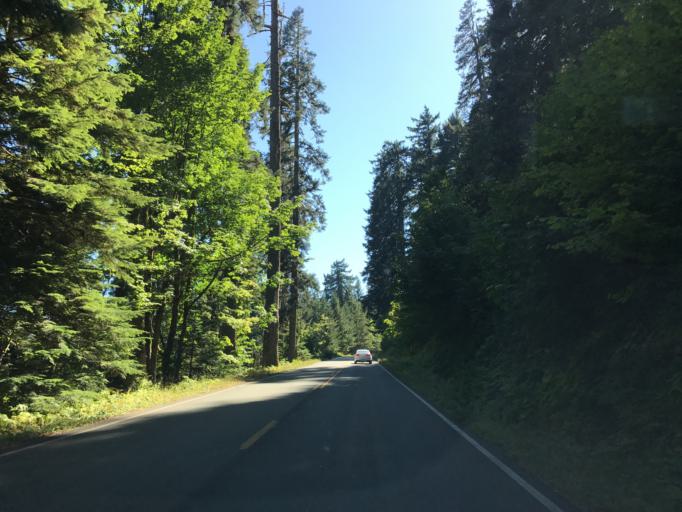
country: US
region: Washington
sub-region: Pierce County
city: Buckley
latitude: 46.7449
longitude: -121.5754
